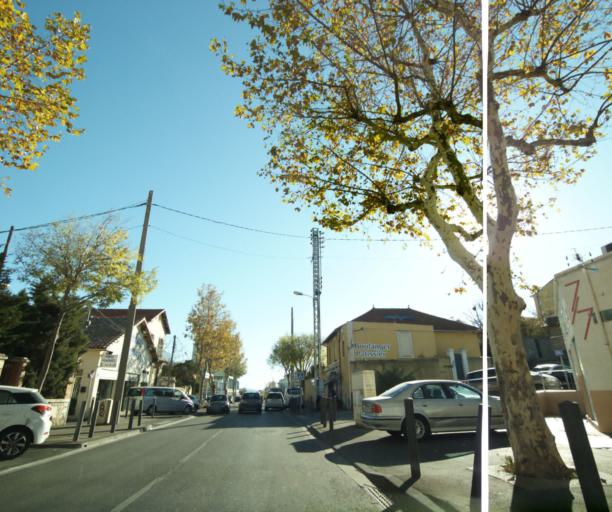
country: FR
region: Provence-Alpes-Cote d'Azur
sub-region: Departement des Bouches-du-Rhone
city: Marseille 15
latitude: 43.3683
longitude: 5.3565
